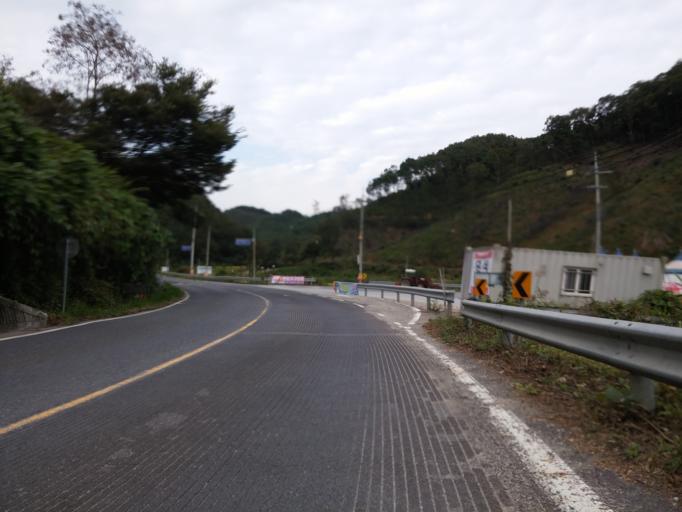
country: KR
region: Daejeon
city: Daejeon
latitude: 36.2217
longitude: 127.2779
